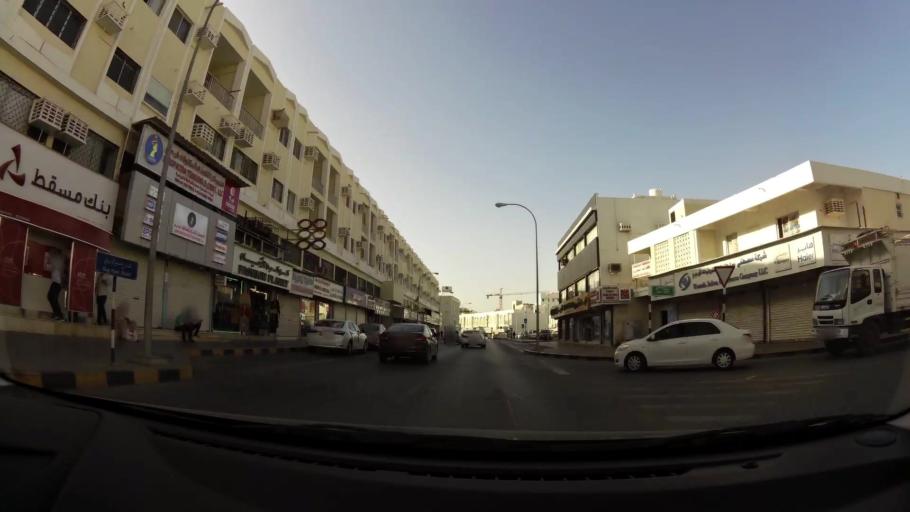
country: OM
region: Muhafazat Masqat
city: Muscat
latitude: 23.5868
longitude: 58.5457
